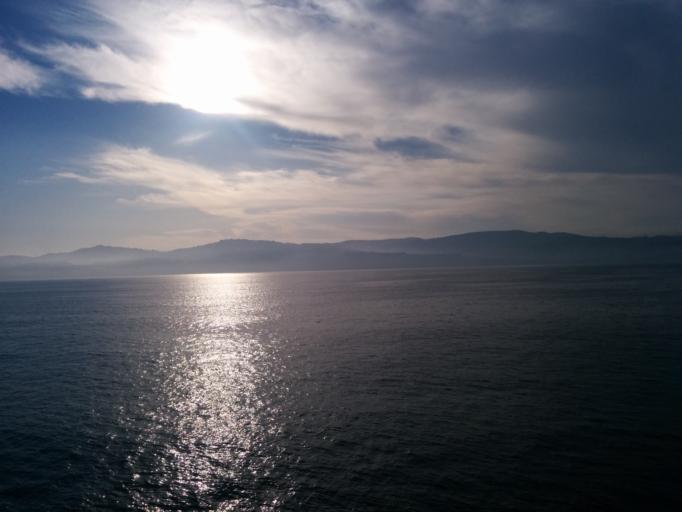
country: MA
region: Tanger-Tetouan
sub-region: Tanger-Assilah
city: Tangier
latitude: 35.8040
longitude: -5.7847
